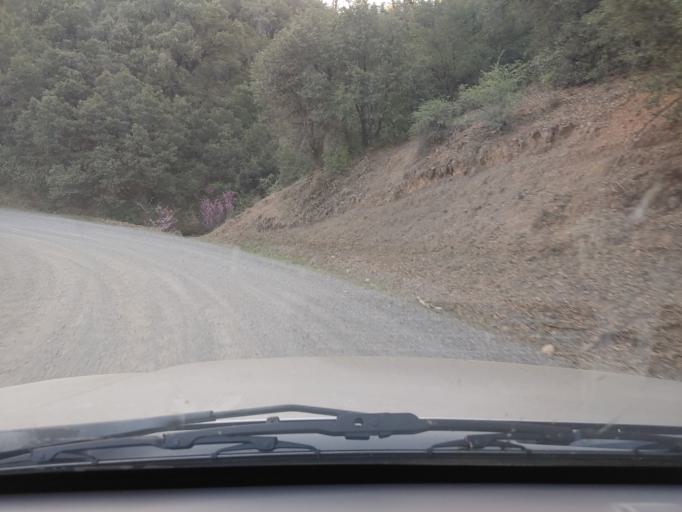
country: US
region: California
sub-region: Shasta County
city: Bella Vista
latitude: 40.8216
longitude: -122.0127
